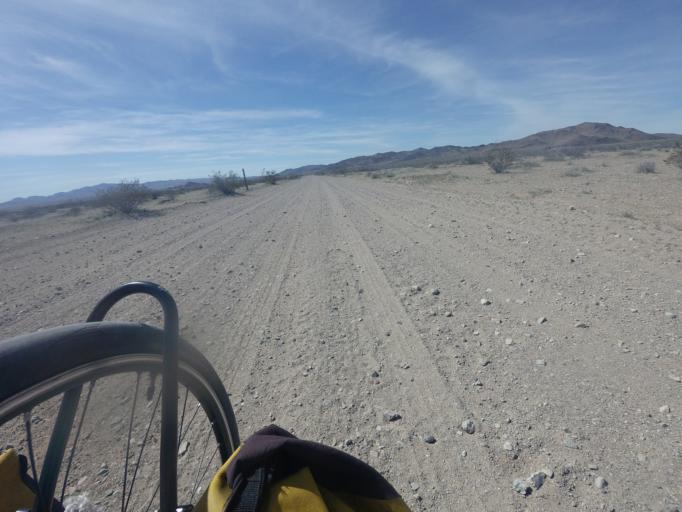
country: US
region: California
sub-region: San Bernardino County
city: Searles Valley
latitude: 35.5986
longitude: -117.3965
